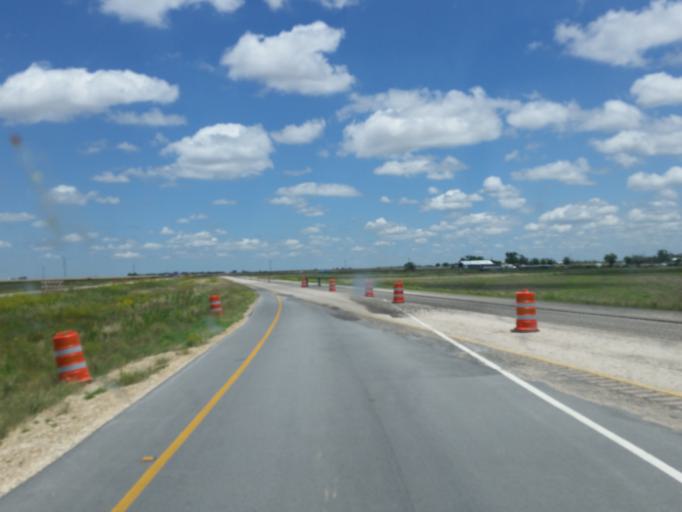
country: US
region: Texas
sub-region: Nolan County
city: Roscoe
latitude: 32.4541
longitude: -100.5462
